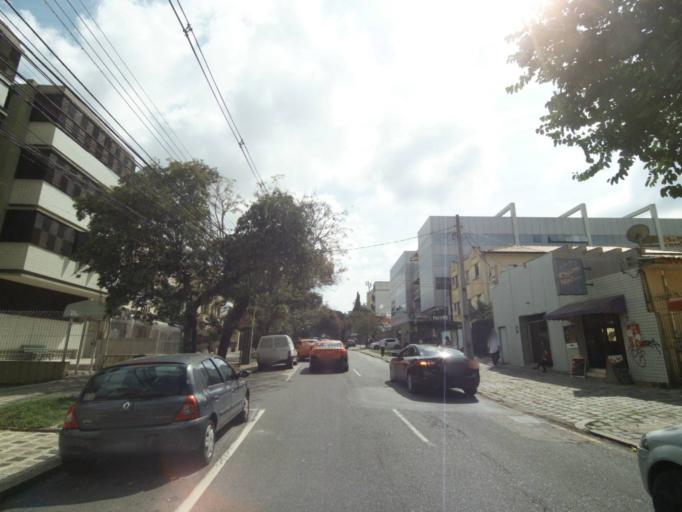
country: BR
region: Parana
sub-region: Curitiba
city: Curitiba
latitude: -25.4258
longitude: -49.2630
